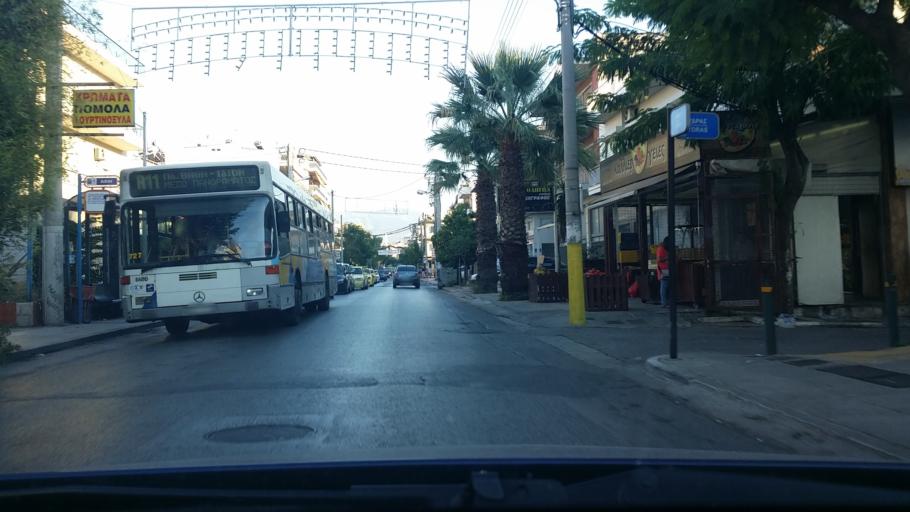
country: GR
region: Attica
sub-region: Nomarchia Athinas
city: Agioi Anargyroi
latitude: 38.0298
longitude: 23.7144
